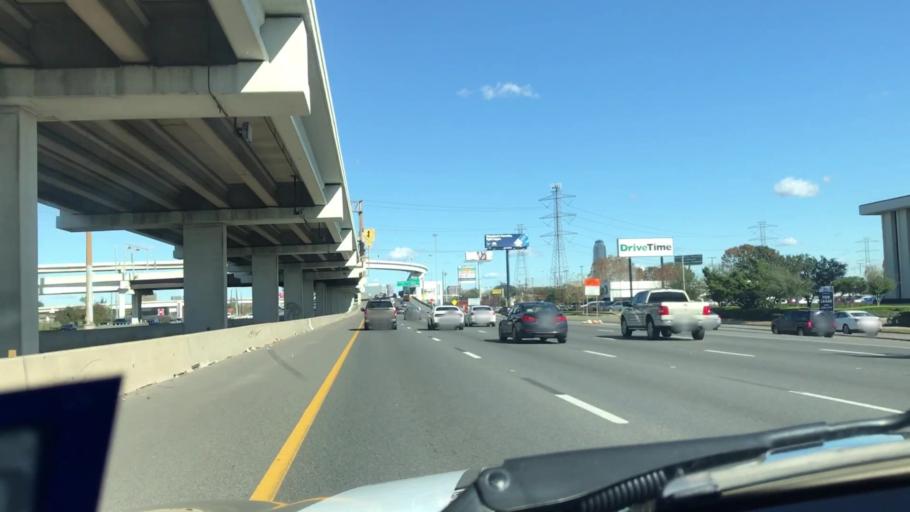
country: US
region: Texas
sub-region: Harris County
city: Bellaire
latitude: 29.7196
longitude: -95.4958
